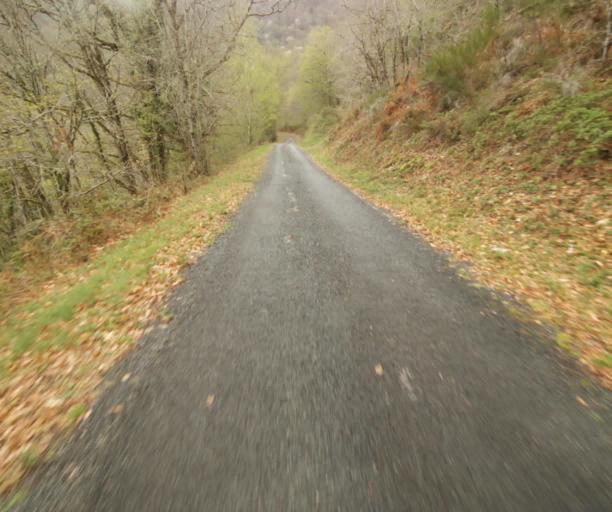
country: FR
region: Limousin
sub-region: Departement de la Correze
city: Saint-Privat
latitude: 45.2062
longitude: 2.0318
